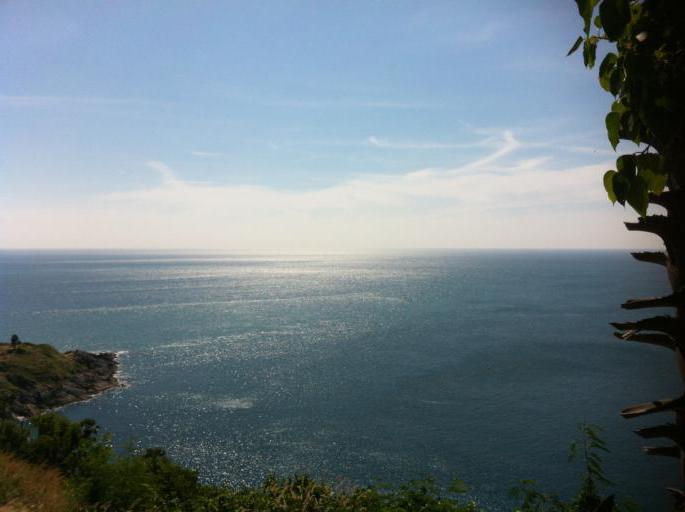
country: TH
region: Phuket
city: Nai Harn
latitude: 7.7628
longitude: 98.3053
